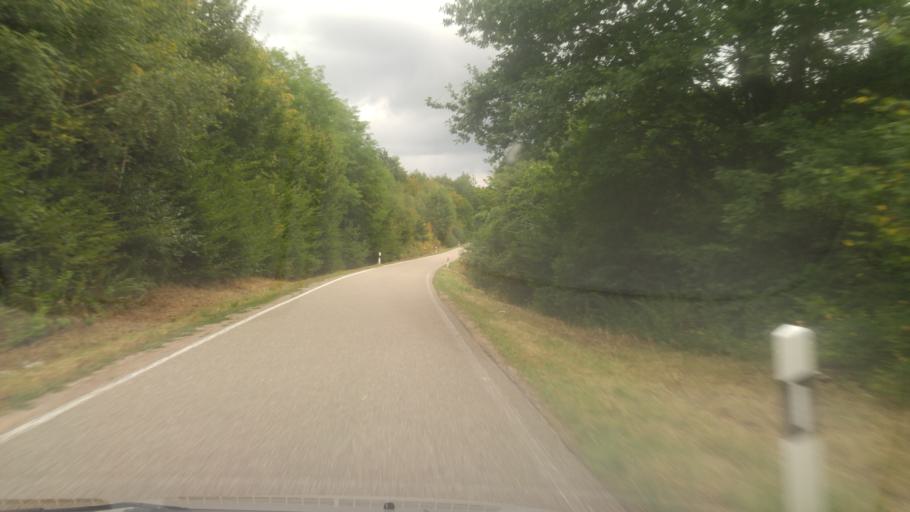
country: DE
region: Rheinland-Pfalz
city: Scheibenhardt
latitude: 48.9873
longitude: 8.1242
